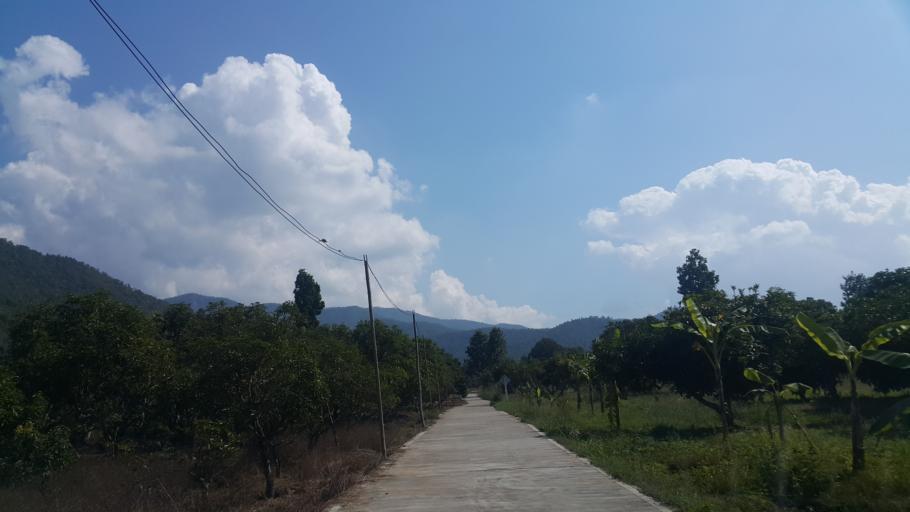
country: TH
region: Lamphun
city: Ban Thi
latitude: 18.6759
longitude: 99.1730
